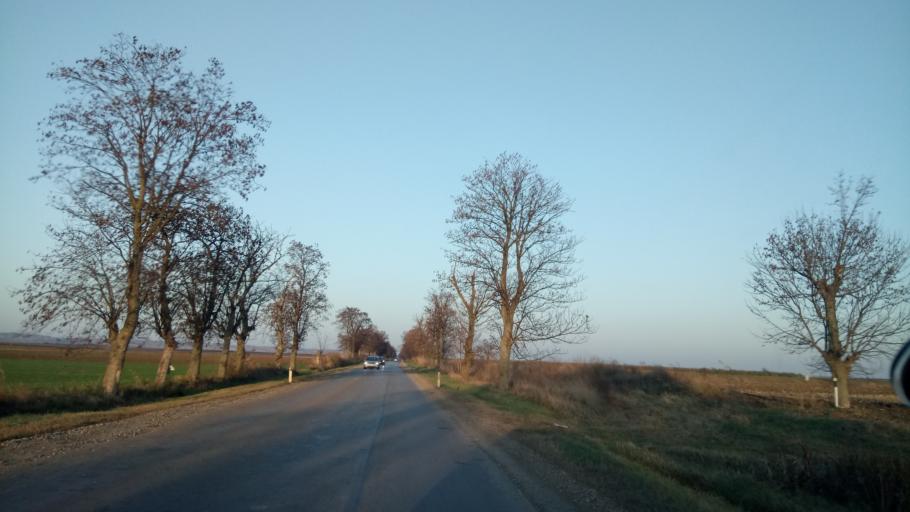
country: RS
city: Novi Karlovci
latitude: 45.0967
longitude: 20.2009
